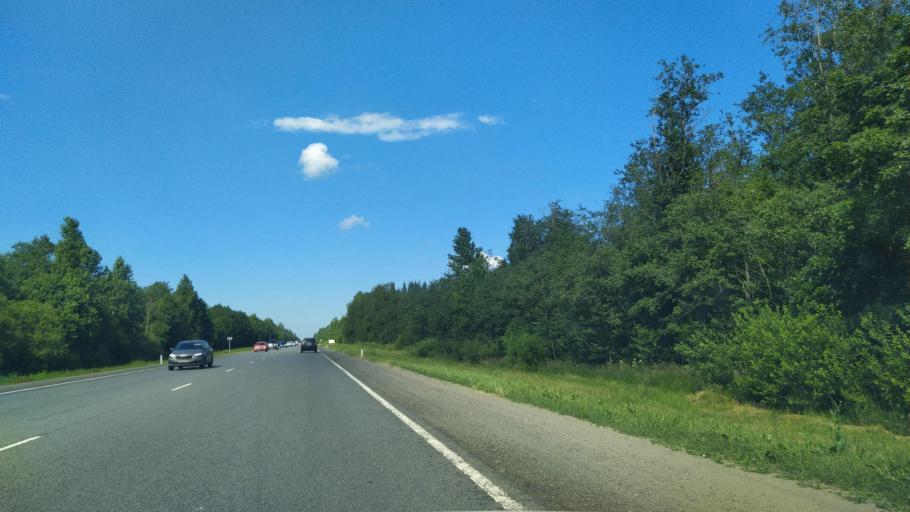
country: RU
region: Leningrad
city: Rozhdestveno
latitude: 59.3568
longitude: 29.9619
